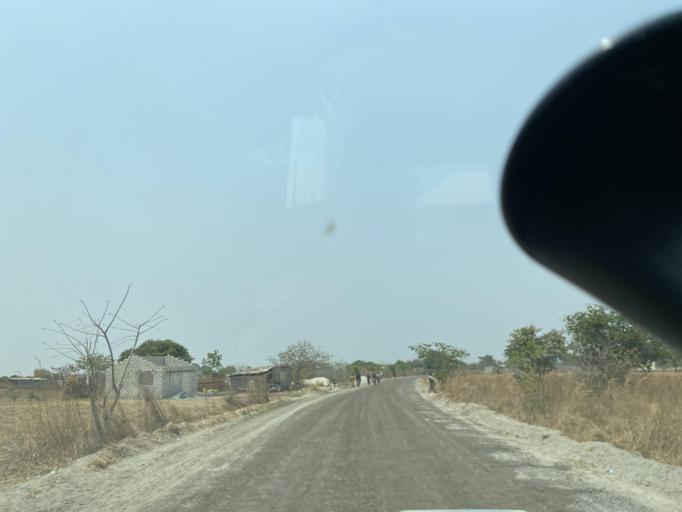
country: ZM
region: Lusaka
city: Lusaka
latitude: -15.5612
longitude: 28.4289
